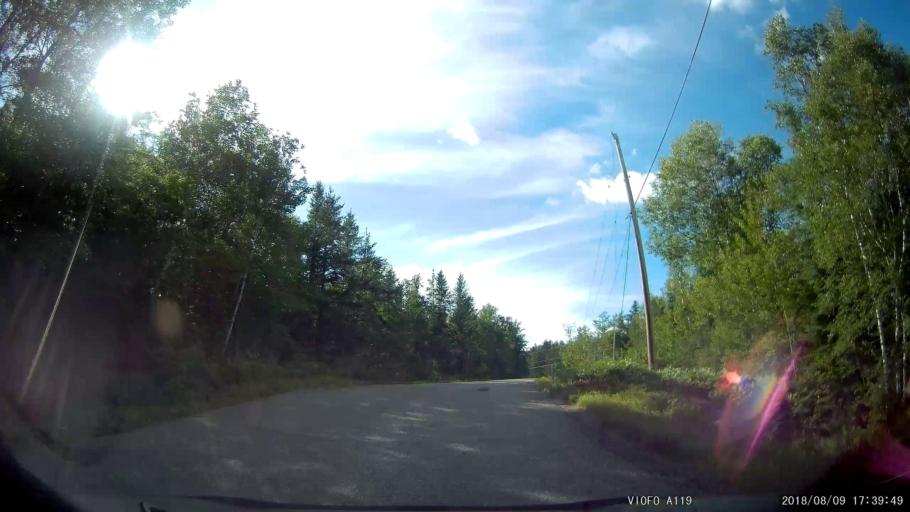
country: CA
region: Ontario
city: Rayside-Balfour
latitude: 46.6051
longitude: -81.4967
